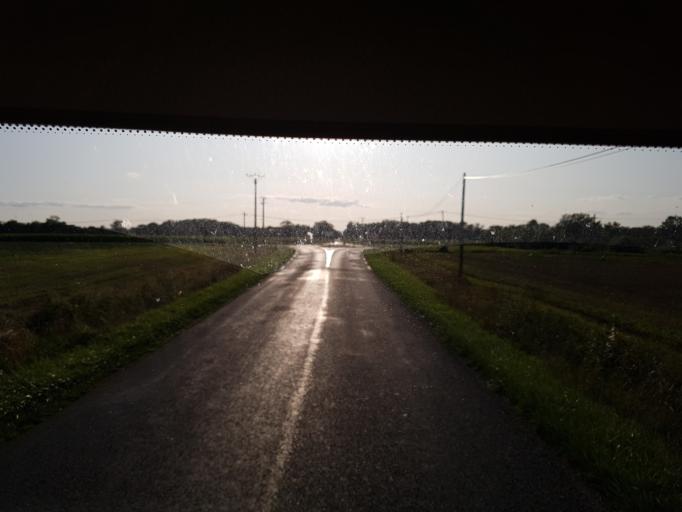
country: FR
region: Rhone-Alpes
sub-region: Departement de l'Ain
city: Villars-les-Dombes
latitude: 45.9631
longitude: 5.0420
